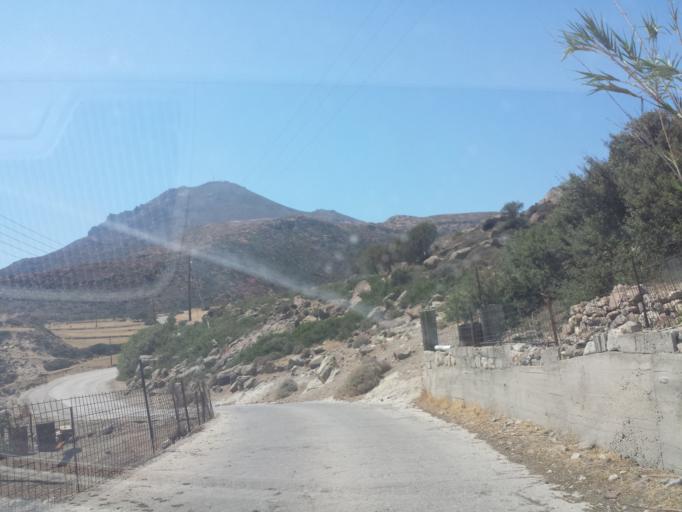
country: GR
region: South Aegean
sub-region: Nomos Kykladon
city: Adamas
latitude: 36.6631
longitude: 24.4139
